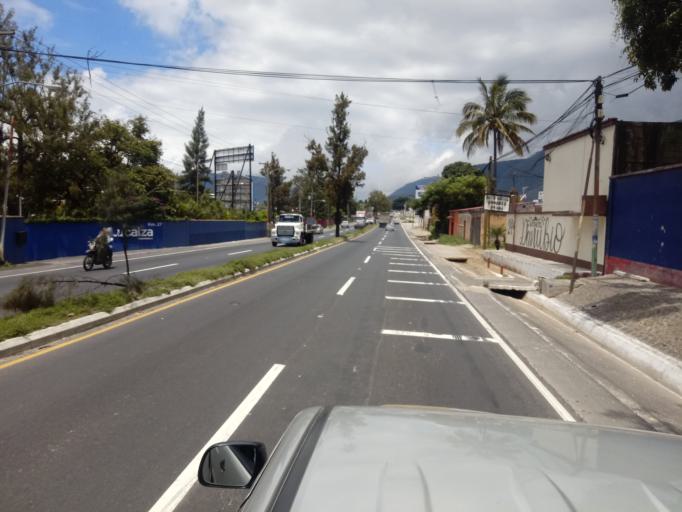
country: GT
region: Guatemala
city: Amatitlan
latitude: 14.4864
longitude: -90.6268
